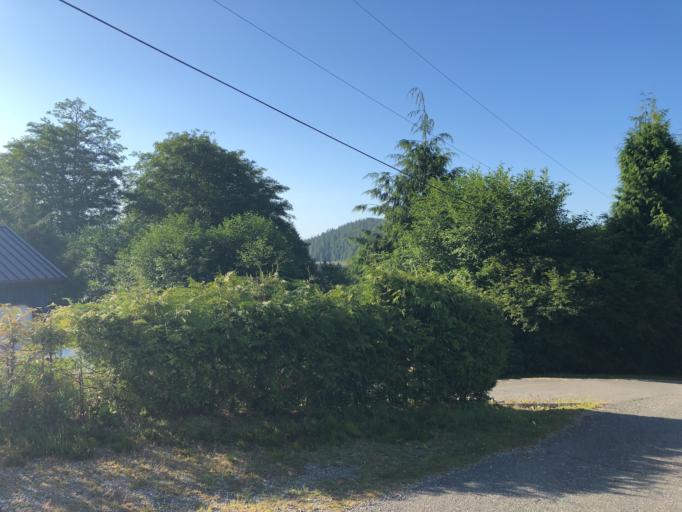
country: CA
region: British Columbia
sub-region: Regional District of Alberni-Clayoquot
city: Ucluelet
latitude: 48.9699
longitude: -125.5895
